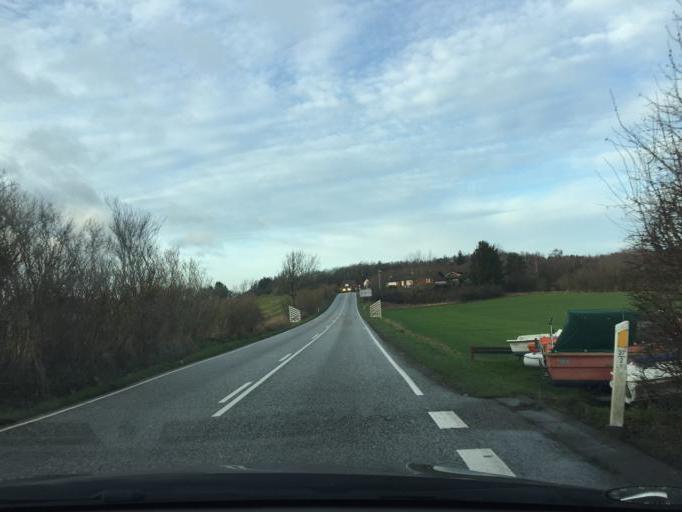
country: DK
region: South Denmark
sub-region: Faaborg-Midtfyn Kommune
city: Ringe
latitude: 55.2060
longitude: 10.4044
